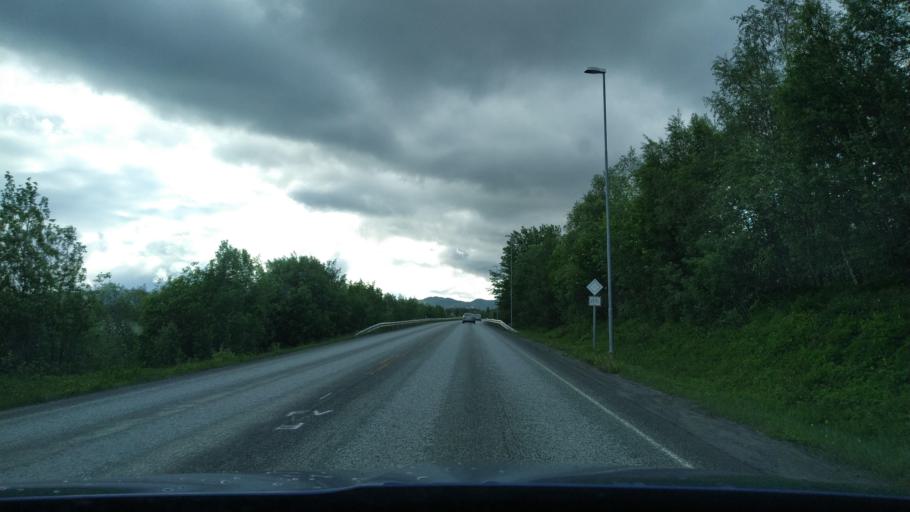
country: NO
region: Troms
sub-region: Lenvik
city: Finnsnes
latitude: 69.2339
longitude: 18.0334
